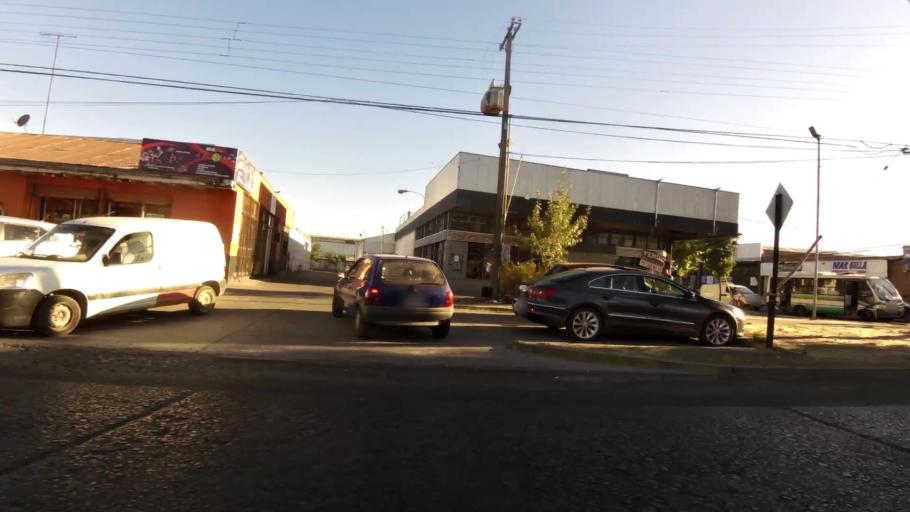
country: CL
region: Maule
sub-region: Provincia de Curico
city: Curico
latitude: -34.9763
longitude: -71.2480
